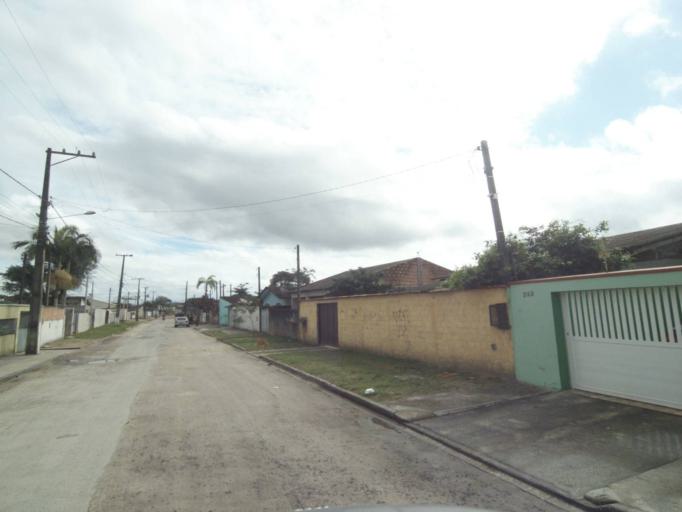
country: BR
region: Parana
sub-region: Paranagua
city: Paranagua
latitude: -25.5710
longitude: -48.5609
